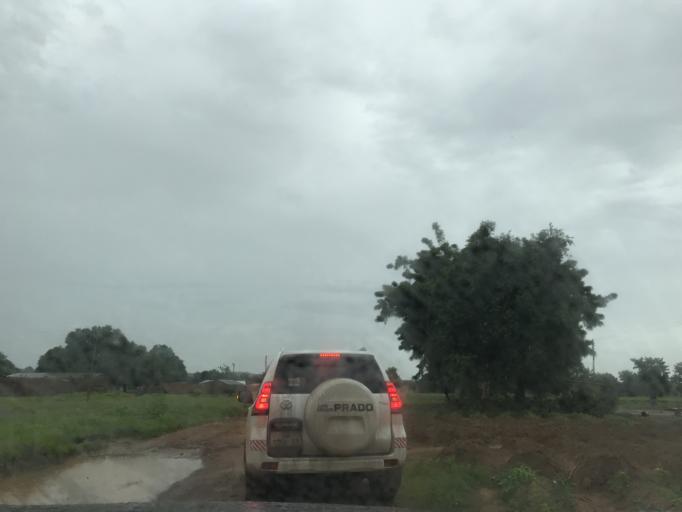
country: GH
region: Upper West
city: Wa
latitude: 10.5111
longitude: -2.7105
